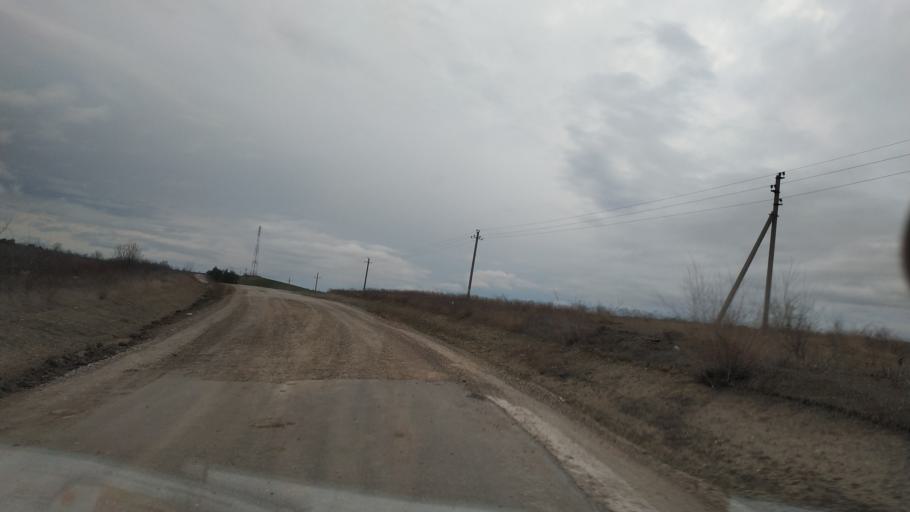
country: MD
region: Causeni
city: Causeni
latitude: 46.6230
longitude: 29.3945
